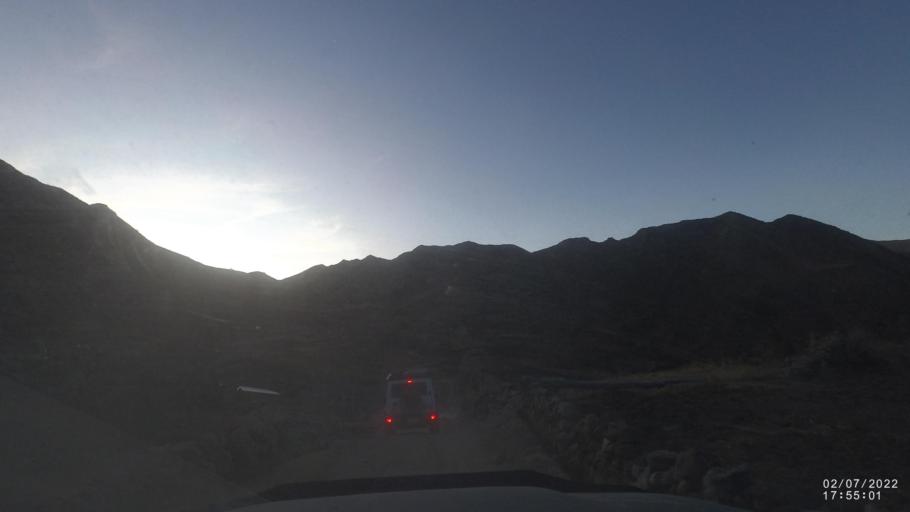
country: BO
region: Cochabamba
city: Irpa Irpa
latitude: -17.8430
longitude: -66.6181
